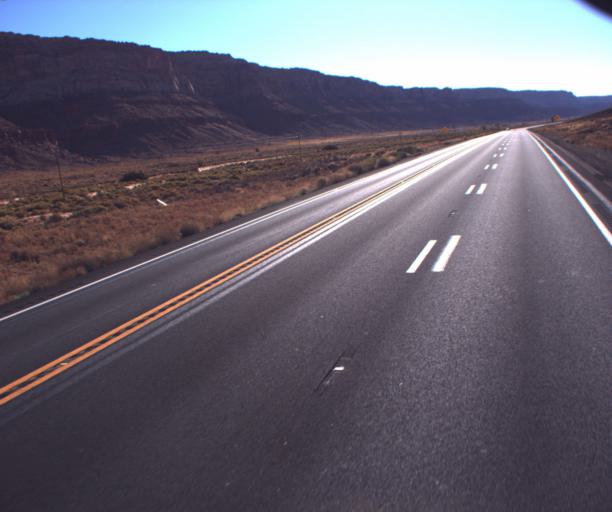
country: US
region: Arizona
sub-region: Coconino County
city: LeChee
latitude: 36.5132
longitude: -111.5894
